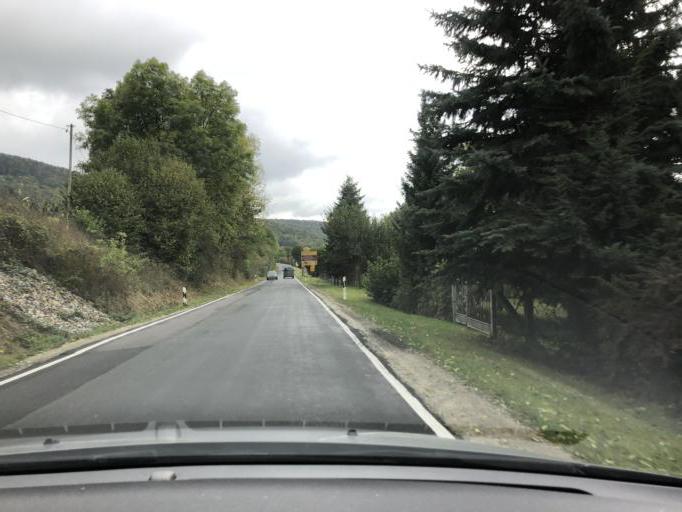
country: DE
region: Thuringia
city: Grossbartloff
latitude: 51.2420
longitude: 10.2063
